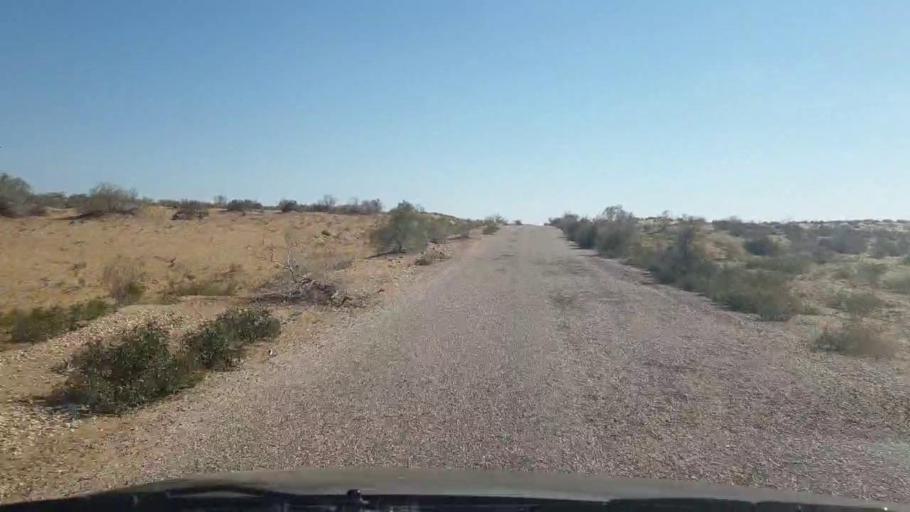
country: PK
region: Sindh
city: Bozdar
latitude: 27.0054
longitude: 68.8034
